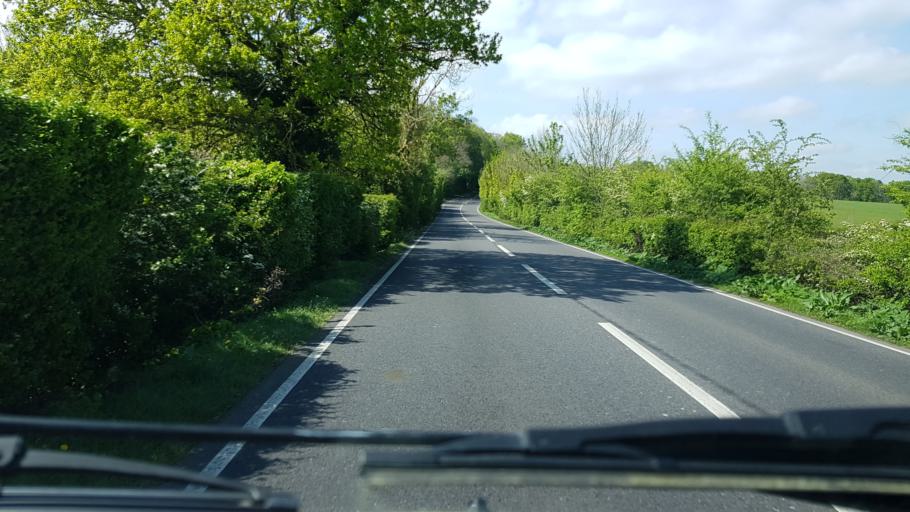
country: GB
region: England
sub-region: Kent
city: Pembury
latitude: 51.1190
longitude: 0.3737
